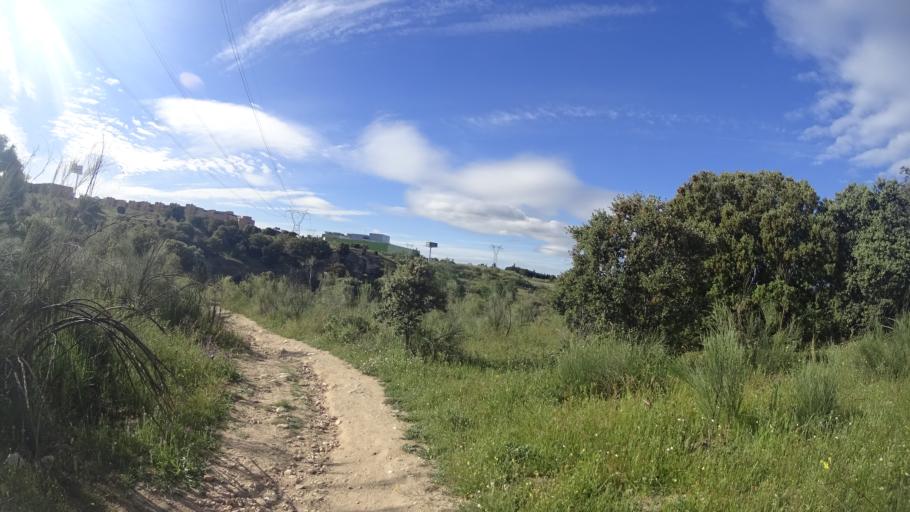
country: ES
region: Madrid
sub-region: Provincia de Madrid
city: Villanueva del Pardillo
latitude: 40.5226
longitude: -3.9360
